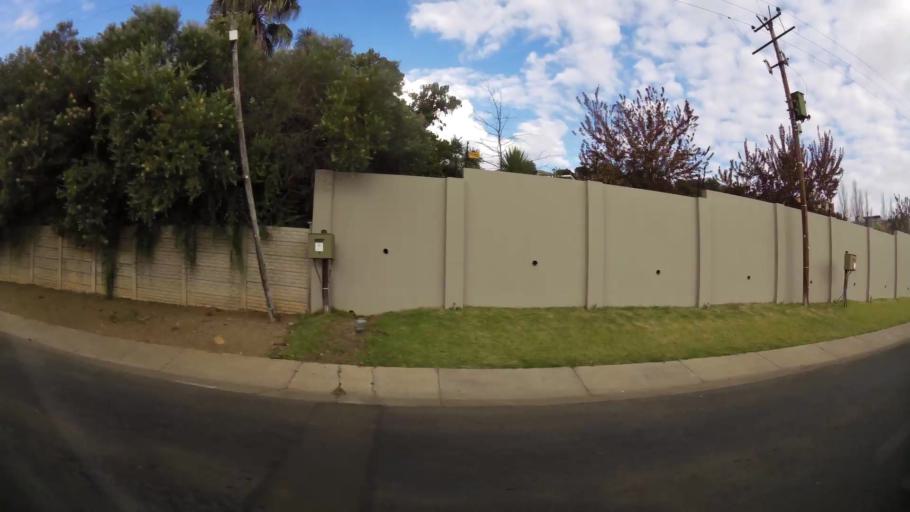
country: ZA
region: Orange Free State
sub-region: Mangaung Metropolitan Municipality
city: Bloemfontein
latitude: -29.0716
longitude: 26.1952
